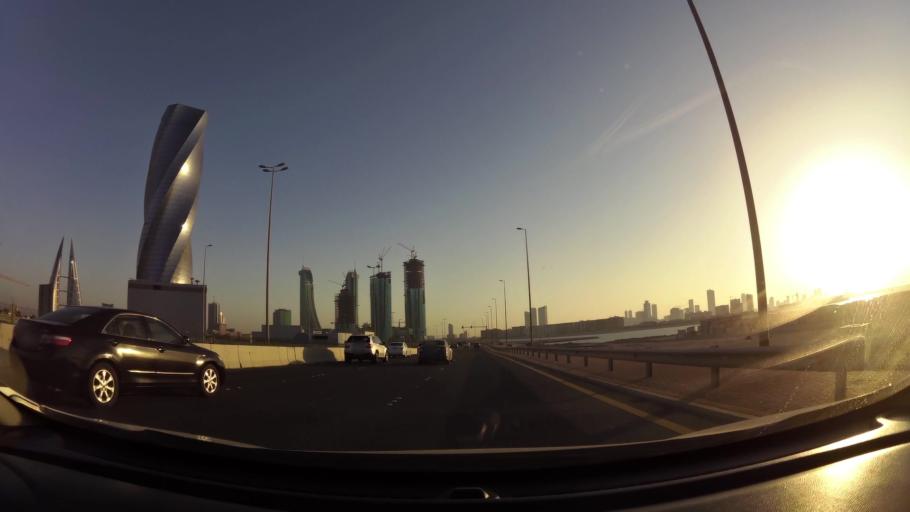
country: BH
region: Manama
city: Manama
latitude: 26.2499
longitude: 50.5763
